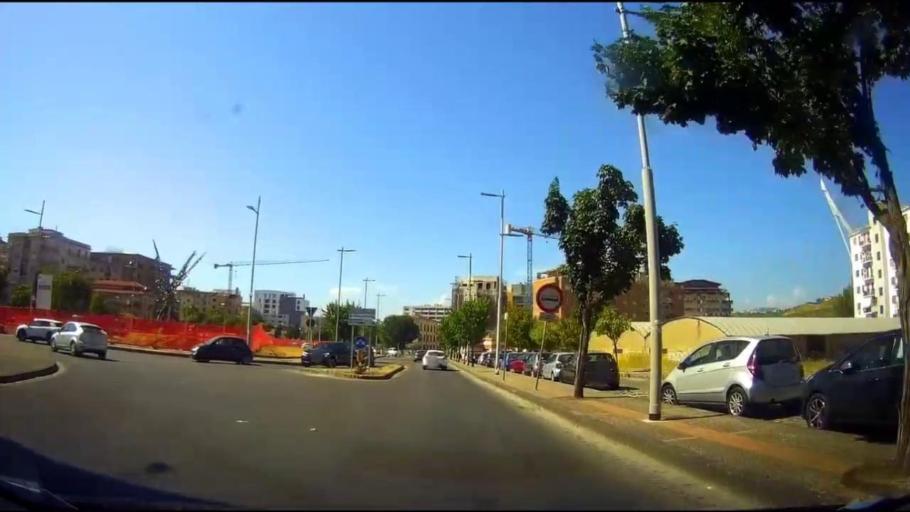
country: IT
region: Calabria
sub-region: Provincia di Cosenza
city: Cosenza
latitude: 39.2960
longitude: 16.2574
